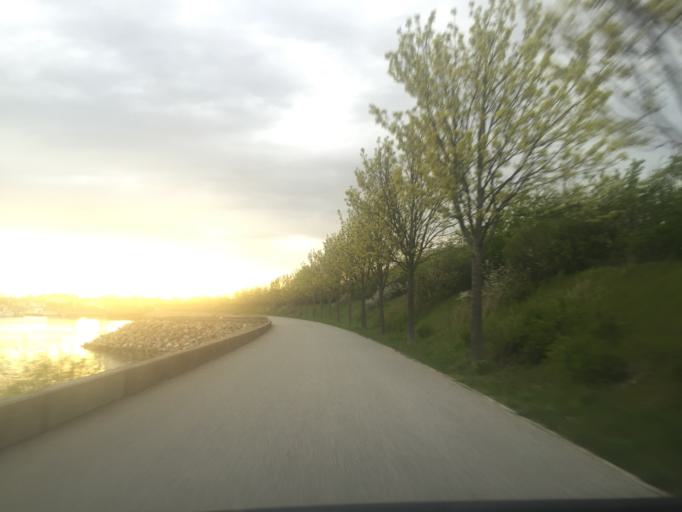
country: DK
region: Capital Region
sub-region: Frederiksberg Kommune
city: Frederiksberg
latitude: 55.6423
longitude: 12.5458
